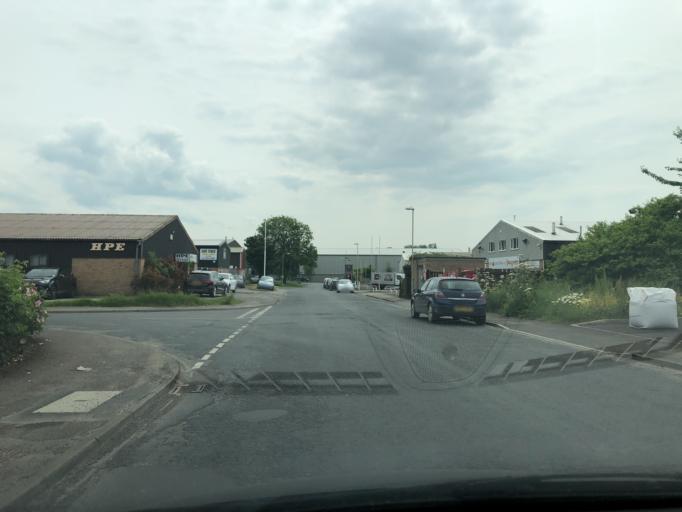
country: GB
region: England
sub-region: North Yorkshire
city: Pickering
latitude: 54.2382
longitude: -0.7598
